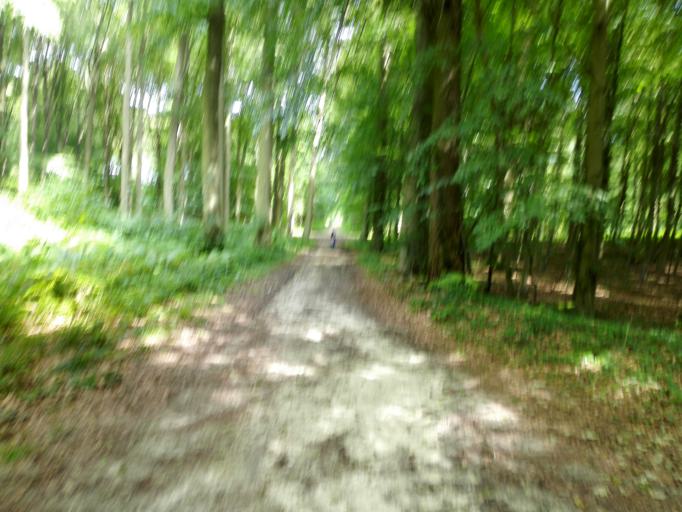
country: BE
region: Flanders
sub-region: Provincie Vlaams-Brabant
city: Oud-Heverlee
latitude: 50.8003
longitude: 4.6817
